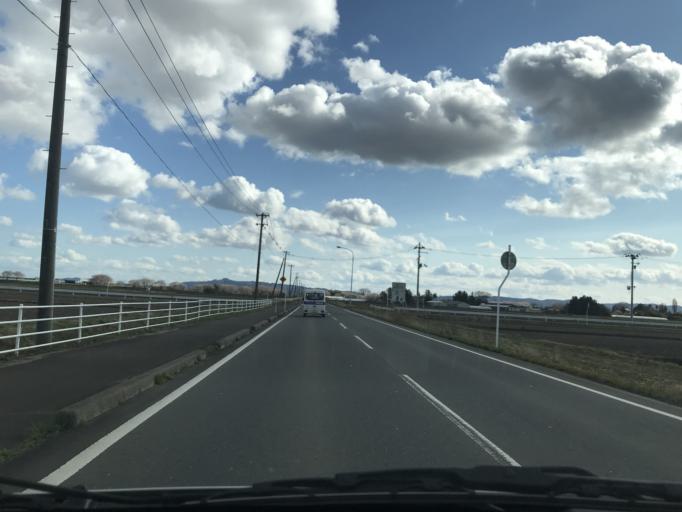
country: JP
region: Miyagi
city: Wakuya
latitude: 38.6489
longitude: 141.1907
